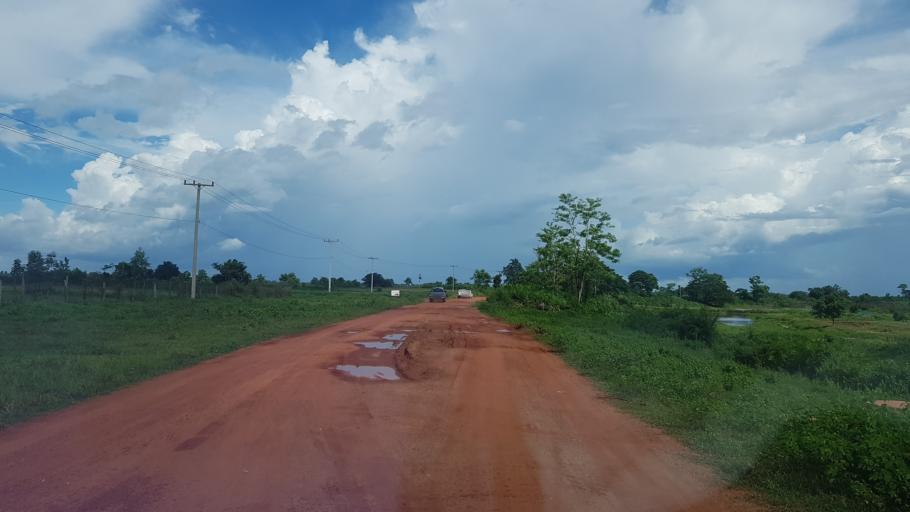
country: LA
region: Vientiane
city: Vientiane
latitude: 18.2358
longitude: 102.5608
